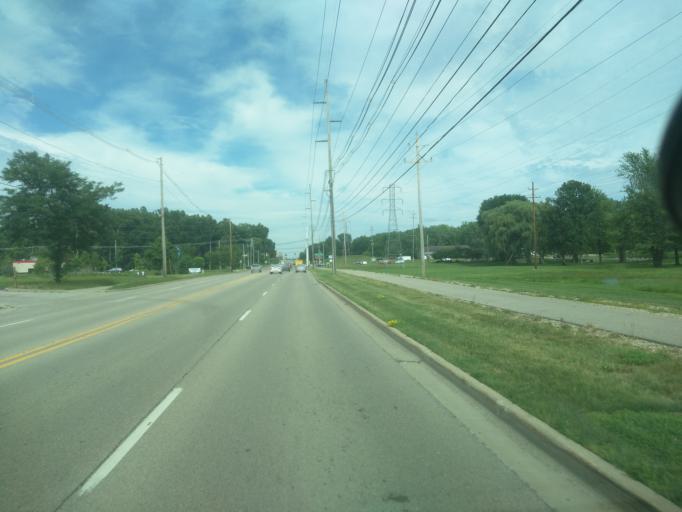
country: US
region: Michigan
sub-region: Ingham County
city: Holt
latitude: 42.6829
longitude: -84.5264
